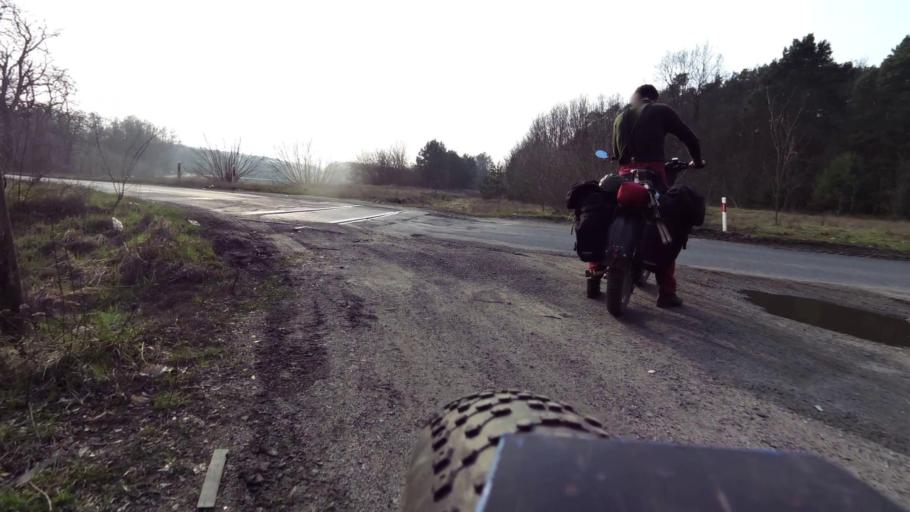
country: PL
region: Lubusz
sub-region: Powiat slubicki
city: Cybinka
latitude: 52.2514
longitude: 14.7361
